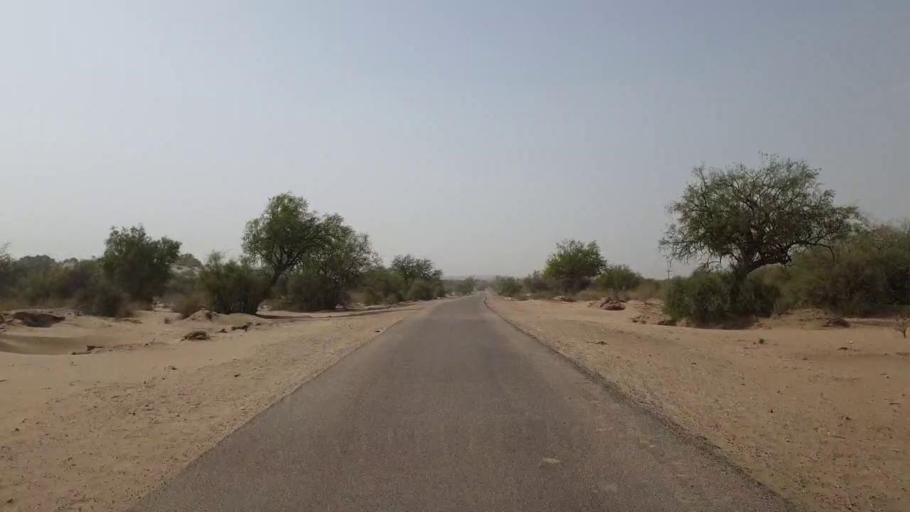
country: PK
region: Sindh
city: Mithi
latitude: 24.6052
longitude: 69.9218
